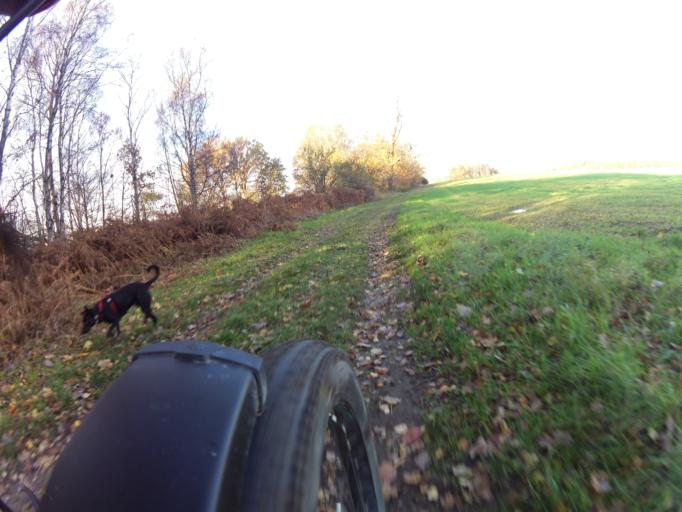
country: PL
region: Pomeranian Voivodeship
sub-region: Powiat pucki
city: Krokowa
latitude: 54.7306
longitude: 18.1981
